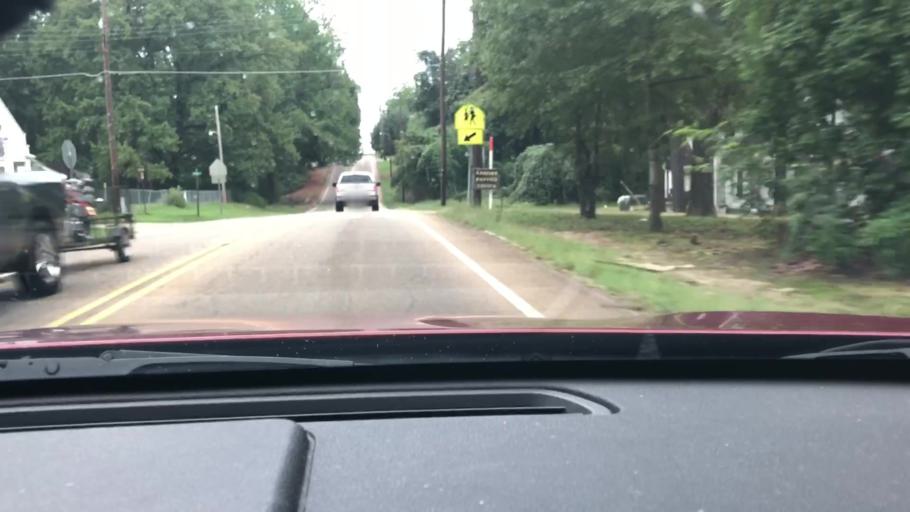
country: US
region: Arkansas
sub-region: Lafayette County
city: Stamps
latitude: 33.3655
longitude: -93.4953
